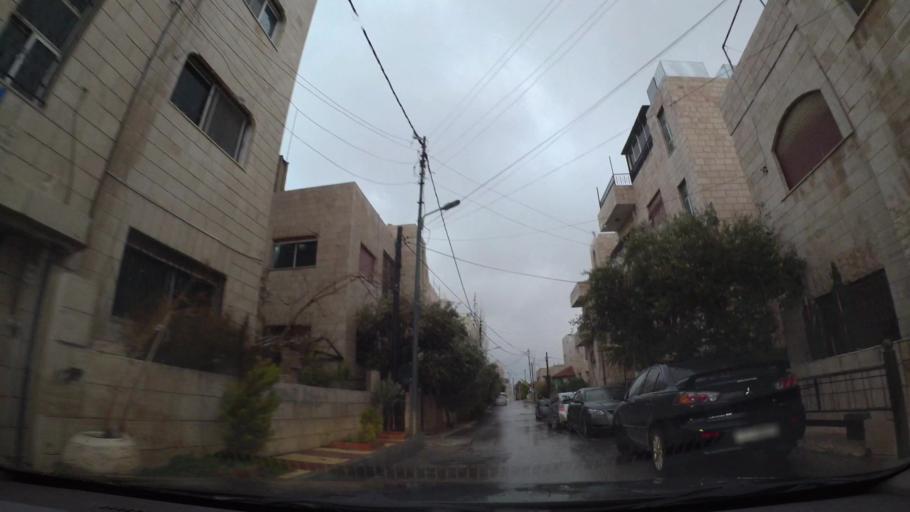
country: JO
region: Amman
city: Amman
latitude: 31.9964
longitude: 35.9198
